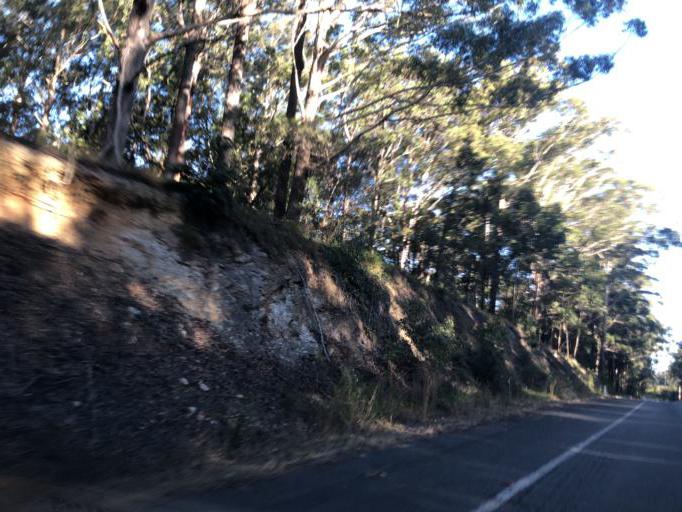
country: AU
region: New South Wales
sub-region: Nambucca Shire
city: Nambucca
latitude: -30.5535
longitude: 153.0072
